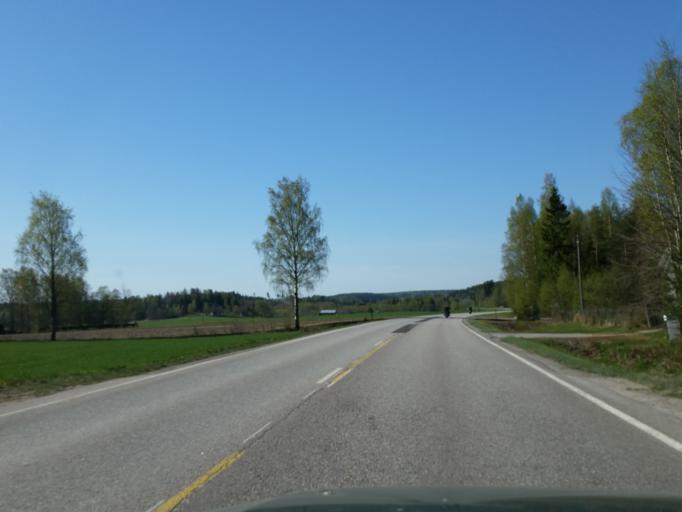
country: FI
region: Uusimaa
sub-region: Helsinki
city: Siuntio
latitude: 60.1867
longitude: 24.2435
